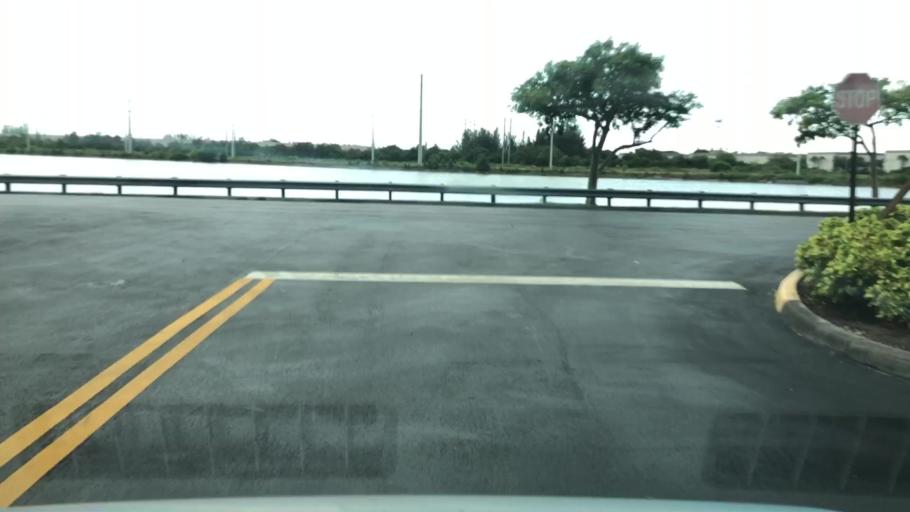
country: US
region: Florida
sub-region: Miami-Dade County
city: Country Club
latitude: 25.9752
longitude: -80.3020
